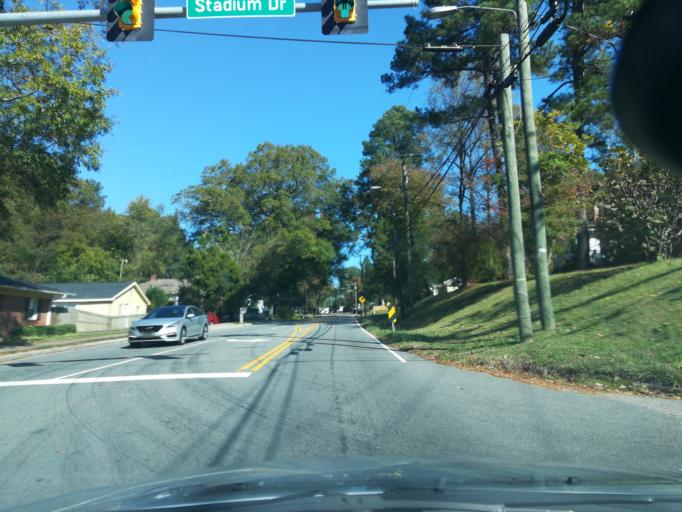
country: US
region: North Carolina
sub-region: Durham County
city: Durham
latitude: 36.0354
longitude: -78.9095
